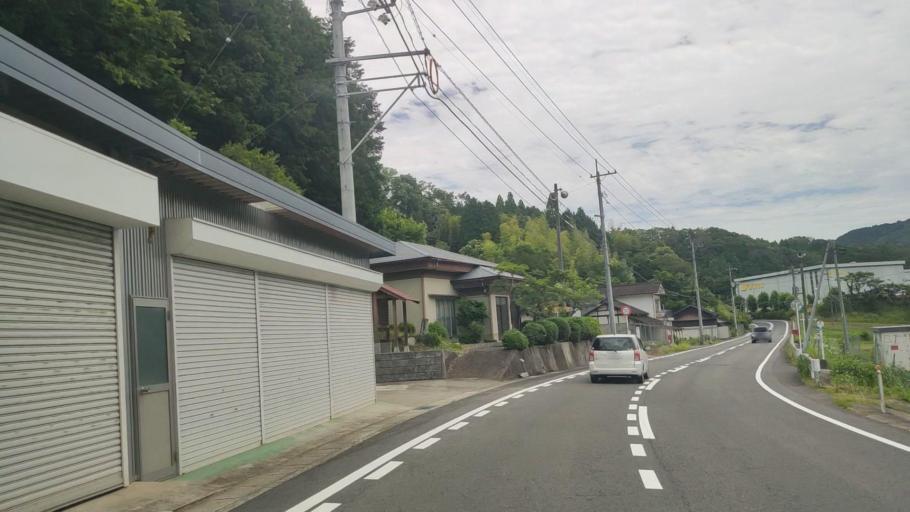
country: JP
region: Hyogo
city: Yamazakicho-nakabirose
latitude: 35.1013
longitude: 134.3146
